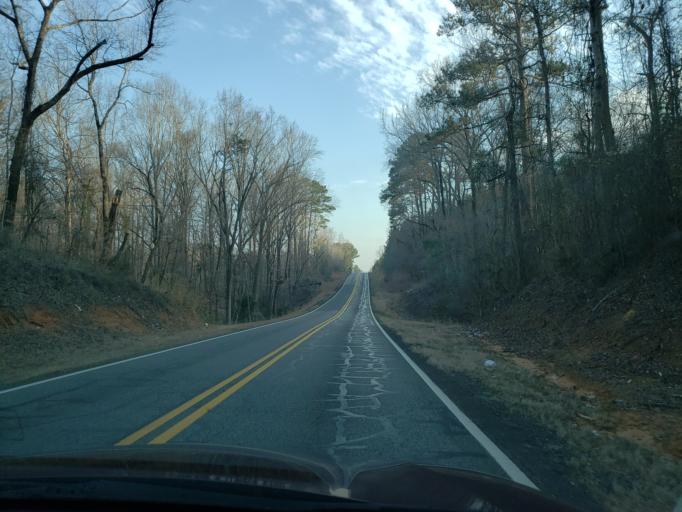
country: US
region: Alabama
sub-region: Hale County
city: Greensboro
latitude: 32.8095
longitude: -87.5947
